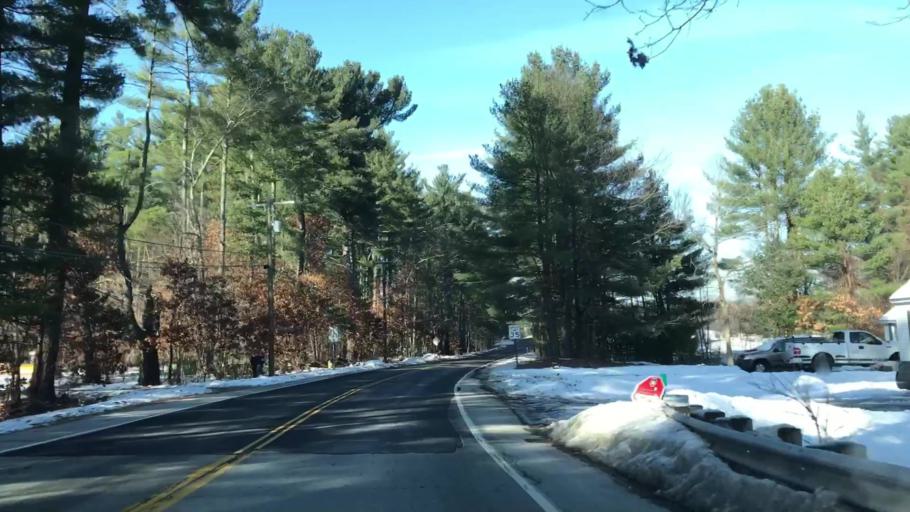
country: US
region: New Hampshire
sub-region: Hillsborough County
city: Milford
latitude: 42.8235
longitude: -71.6066
